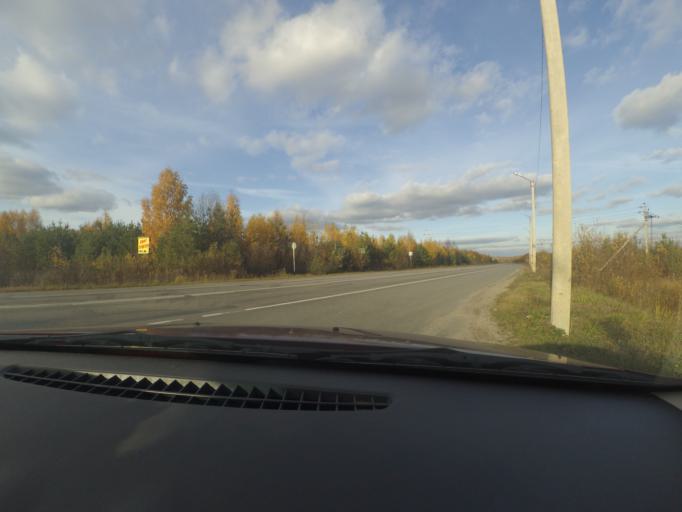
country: RU
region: Vladimir
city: Melenki
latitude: 55.3250
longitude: 41.6523
